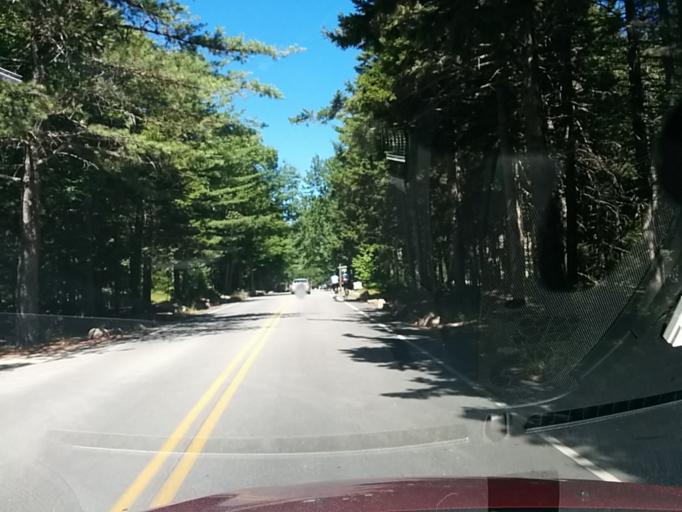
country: US
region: Maine
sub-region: Hancock County
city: Bar Harbor
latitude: 44.3185
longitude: -68.2519
